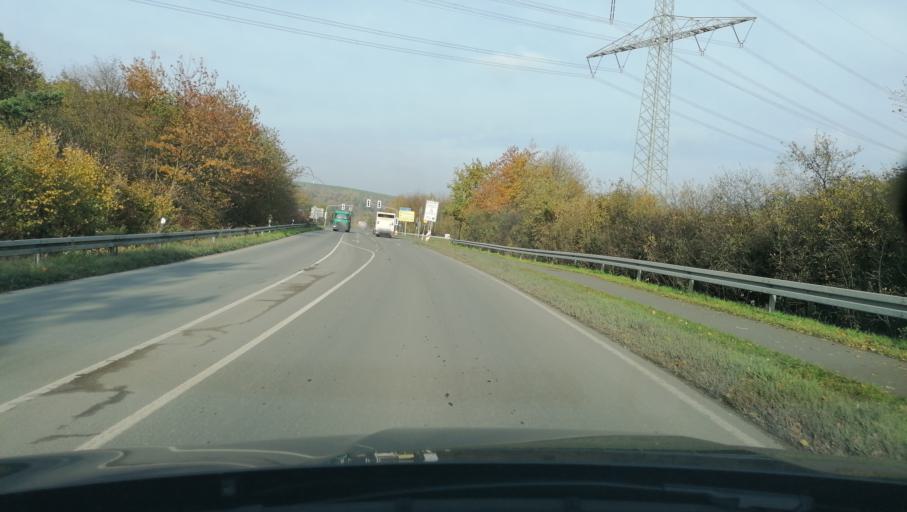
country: DE
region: North Rhine-Westphalia
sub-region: Regierungsbezirk Arnsberg
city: Herne
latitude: 51.5553
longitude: 7.1768
